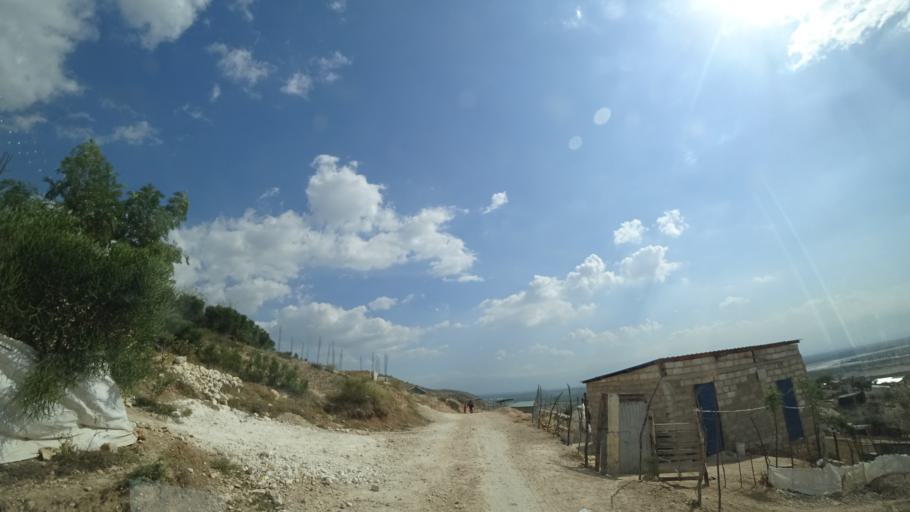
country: HT
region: Ouest
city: Cabaret
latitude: 18.6773
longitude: -72.3101
